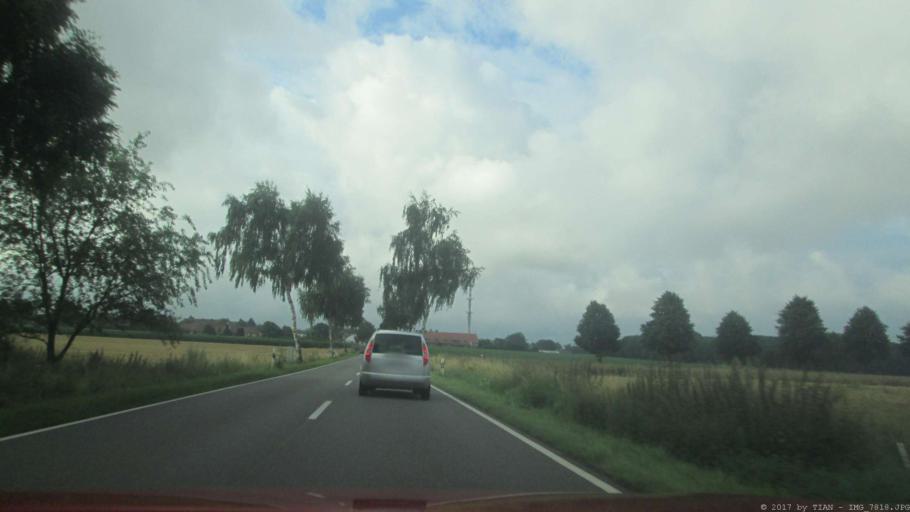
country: DE
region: Lower Saxony
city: Wittingen
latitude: 52.7415
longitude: 10.7351
